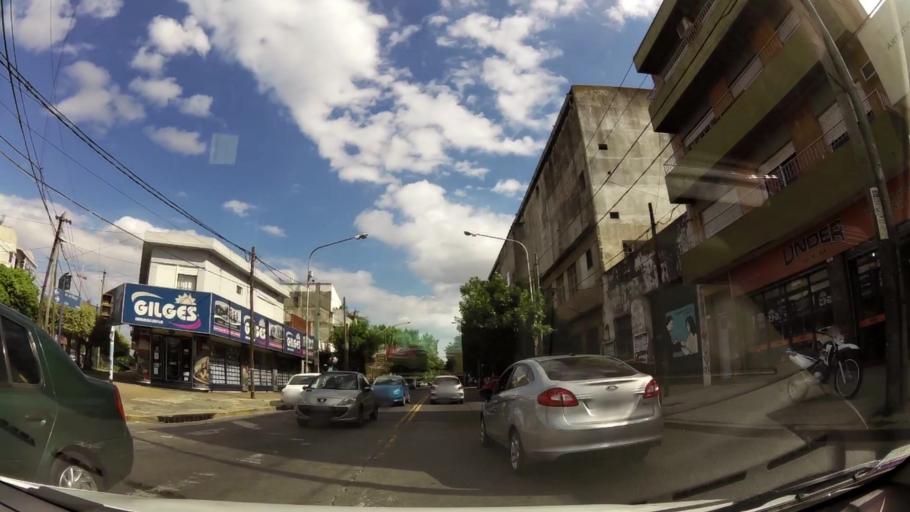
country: AR
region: Buenos Aires
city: San Justo
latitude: -34.6648
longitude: -58.5612
